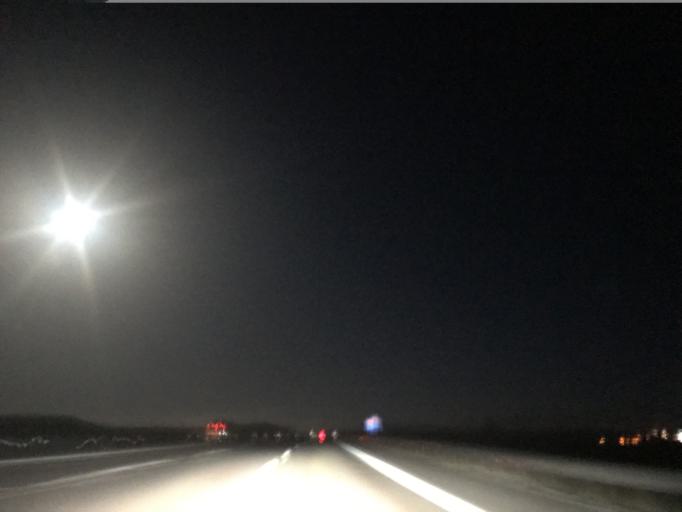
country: TR
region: Nigde
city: Ulukisla
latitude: 37.6457
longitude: 34.3686
